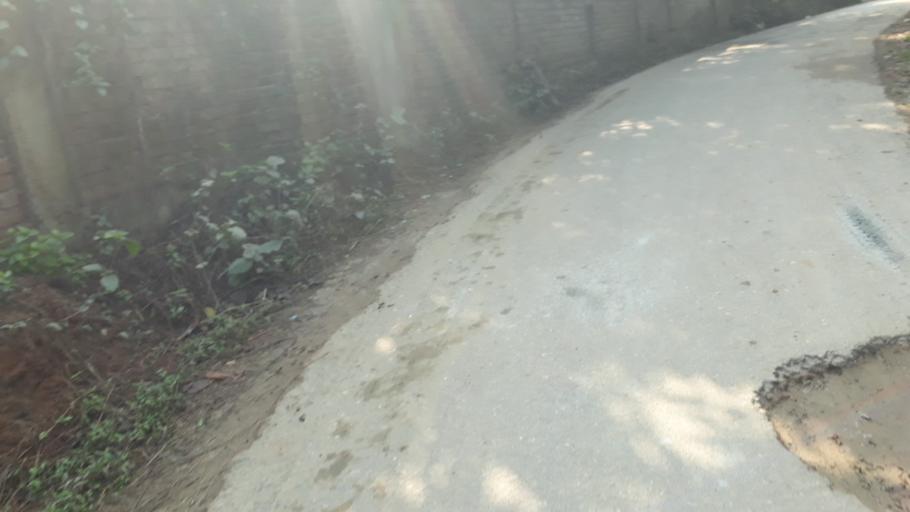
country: BD
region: Dhaka
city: Tungi
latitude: 23.8740
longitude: 90.2597
